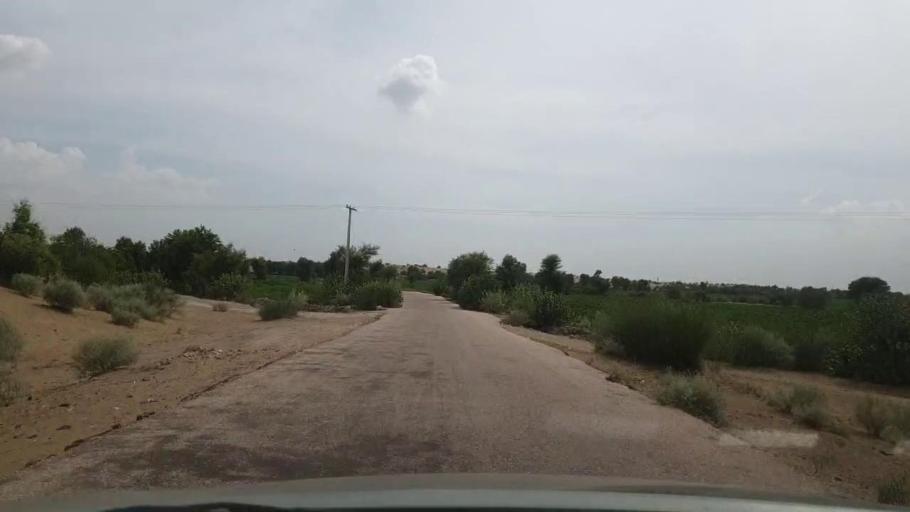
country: PK
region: Sindh
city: Kot Diji
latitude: 27.1646
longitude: 69.0356
